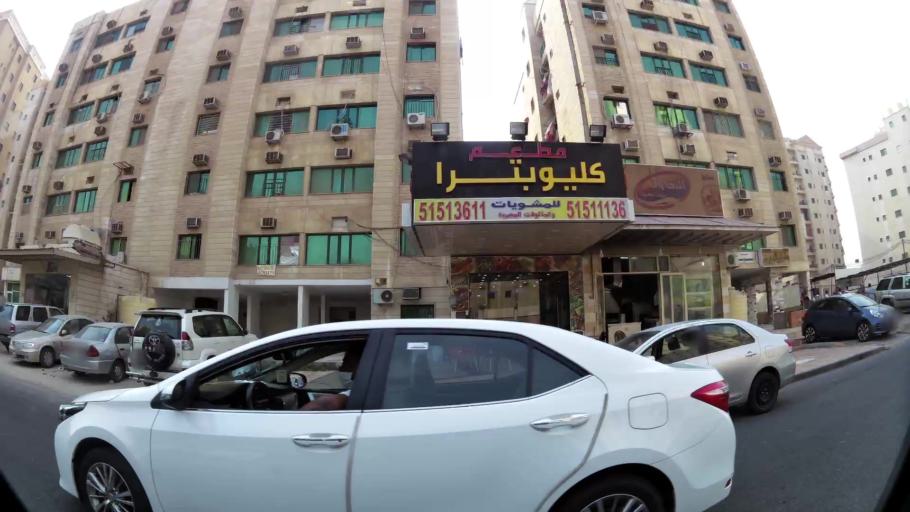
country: KW
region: Al Farwaniyah
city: Al Farwaniyah
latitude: 29.2770
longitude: 47.9547
